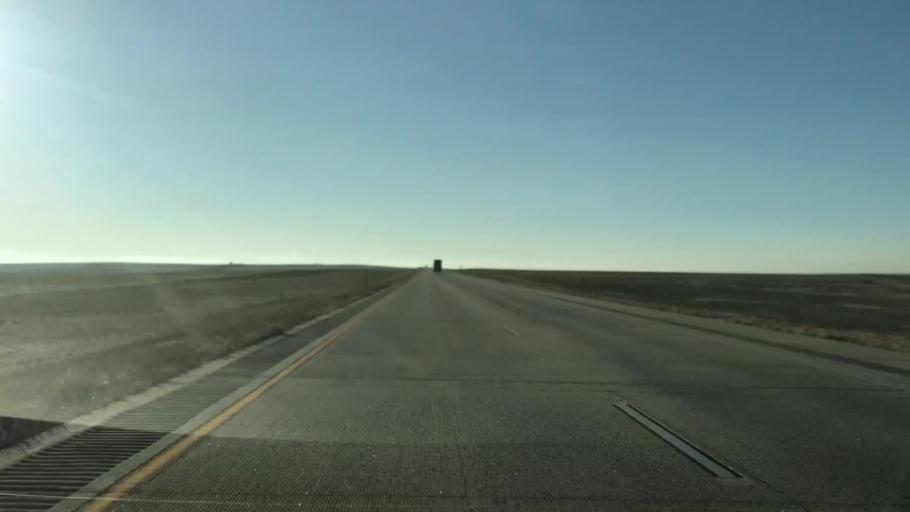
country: US
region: Colorado
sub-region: Lincoln County
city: Limon
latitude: 39.4173
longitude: -103.9081
